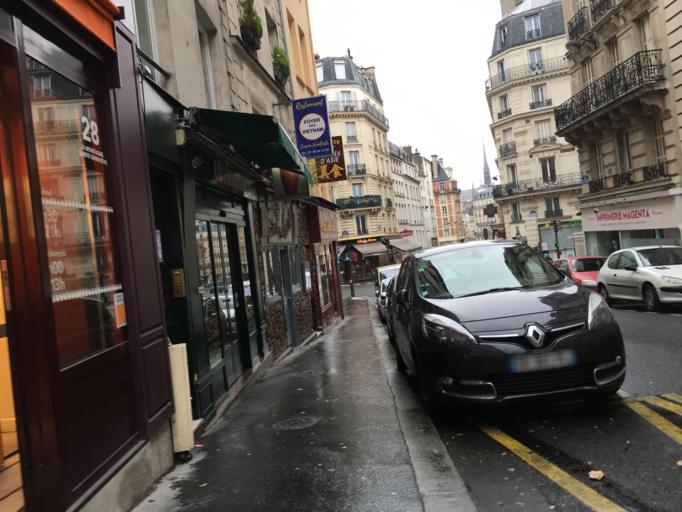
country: FR
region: Ile-de-France
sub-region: Paris
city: Paris
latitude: 48.8482
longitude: 2.3485
